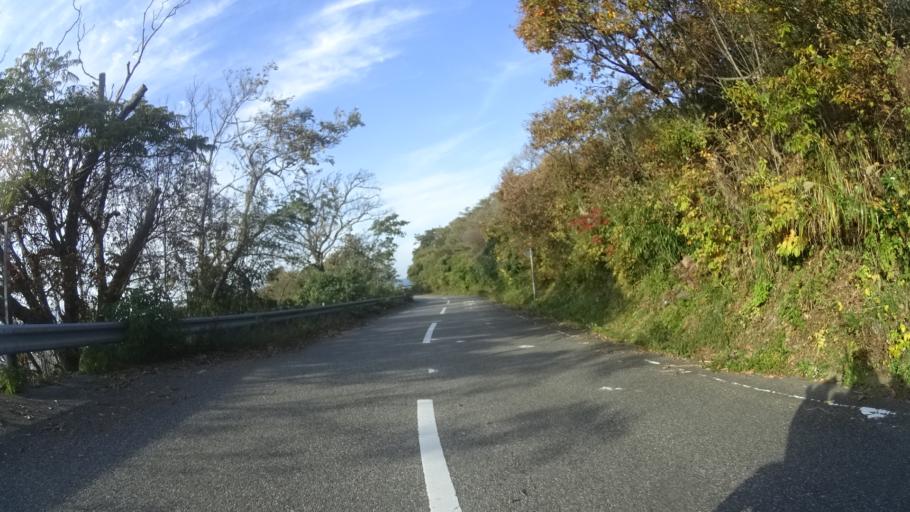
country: JP
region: Ishikawa
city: Hakui
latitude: 37.0914
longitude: 136.7279
